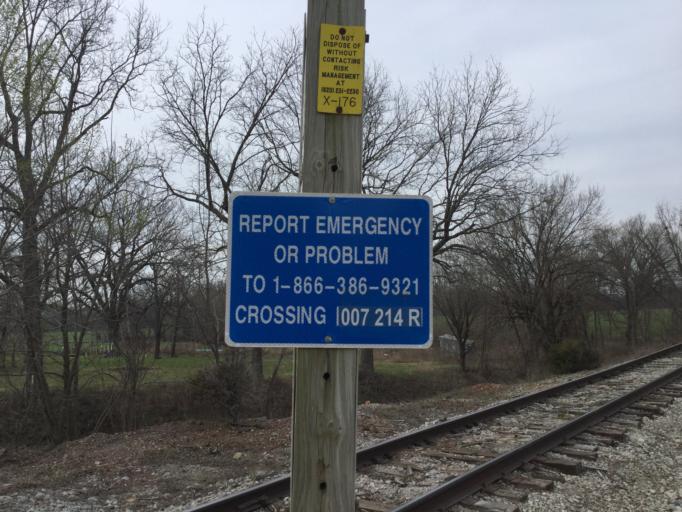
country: US
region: Kansas
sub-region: Wilson County
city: Fredonia
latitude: 37.5158
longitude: -95.8466
